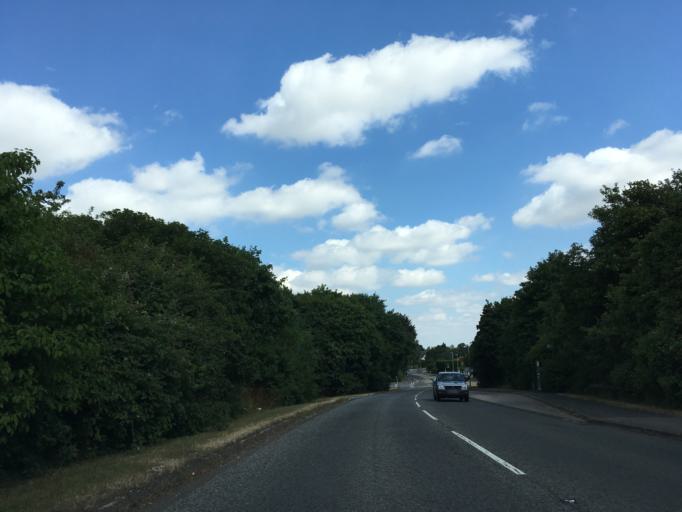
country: GB
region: England
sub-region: Gloucestershire
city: Barnwood
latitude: 51.8856
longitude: -2.2141
